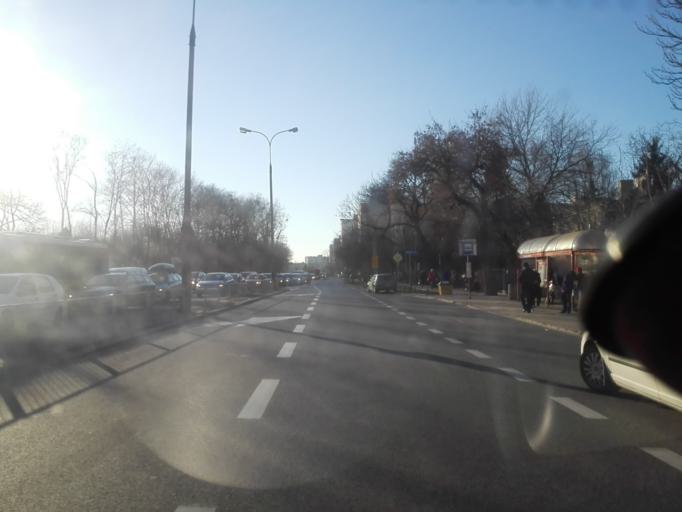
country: PL
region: Masovian Voivodeship
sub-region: Warszawa
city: Mokotow
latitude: 52.1735
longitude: 21.0194
